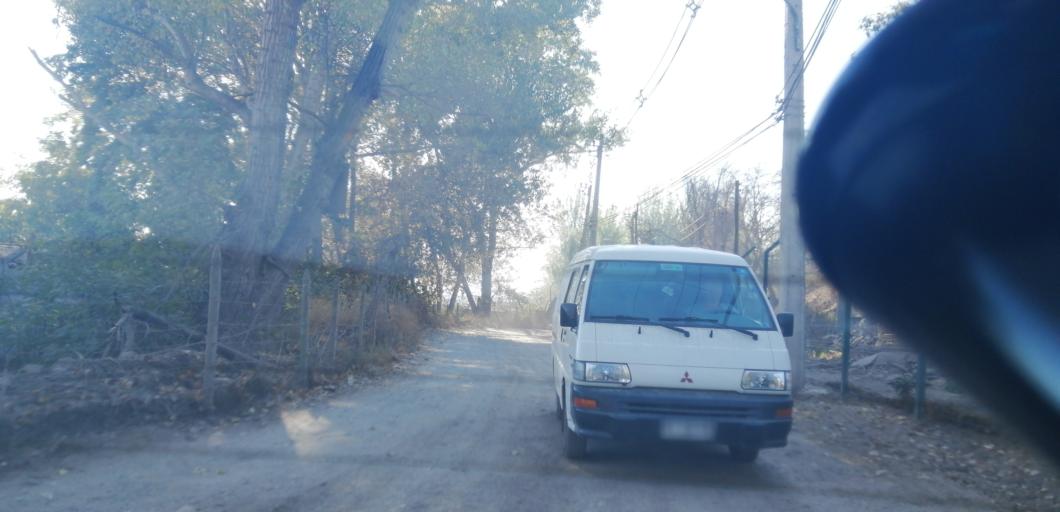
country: CL
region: Santiago Metropolitan
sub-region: Provincia de Santiago
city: Lo Prado
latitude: -33.4632
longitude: -70.7744
